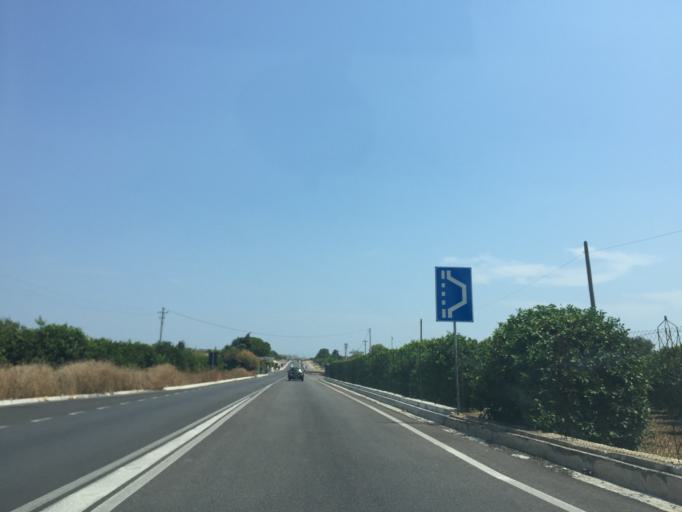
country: IT
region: Sicily
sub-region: Provincia di Siracusa
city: Belvedere
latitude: 37.0719
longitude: 15.2286
